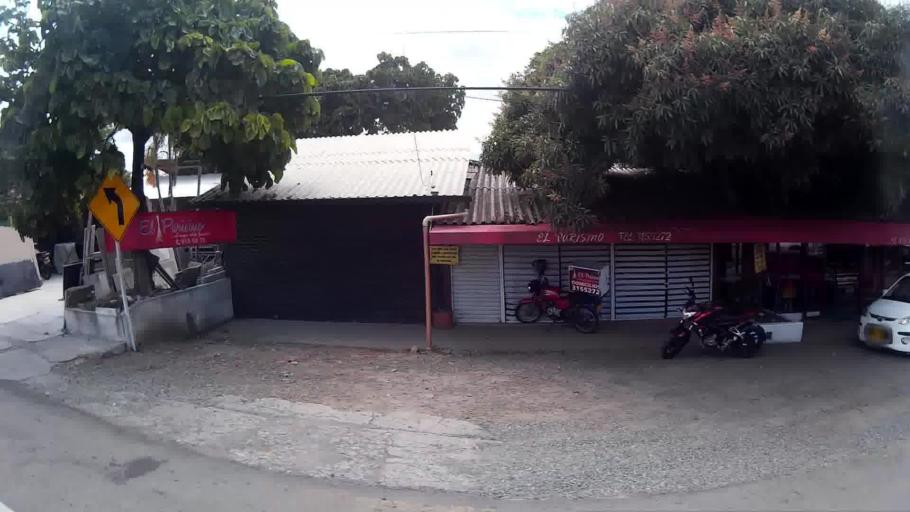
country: CO
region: Risaralda
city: Pereira
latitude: 4.8115
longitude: -75.7725
